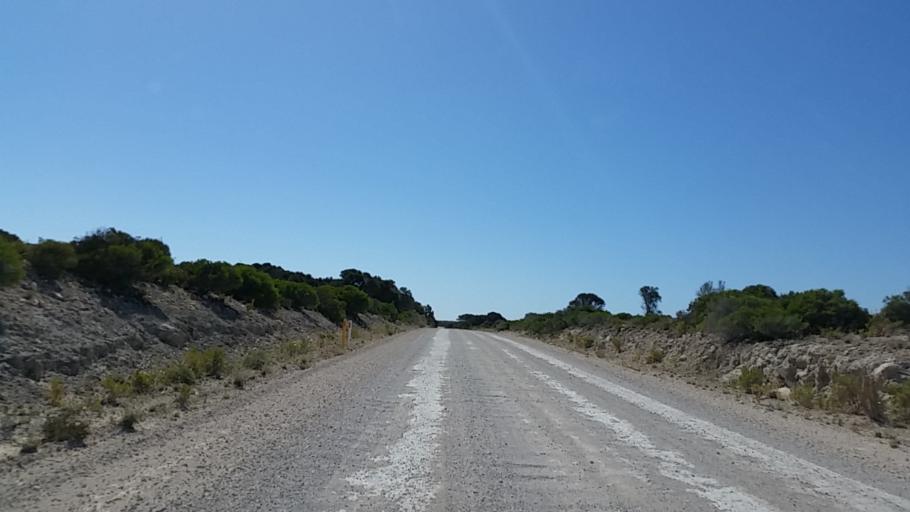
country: AU
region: South Australia
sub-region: Yorke Peninsula
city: Honiton
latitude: -35.2181
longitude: 137.0507
